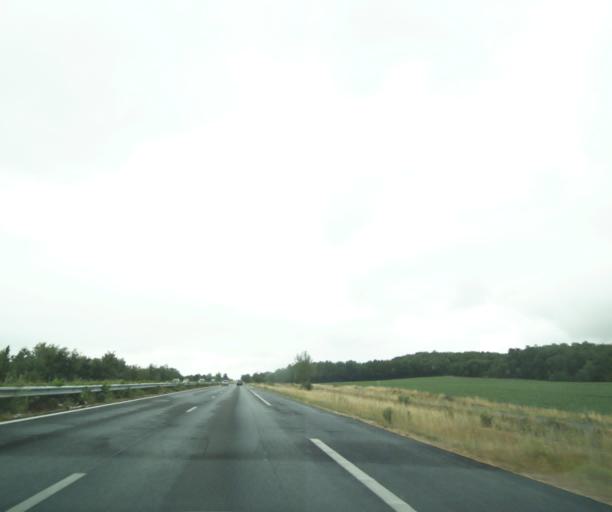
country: FR
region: Midi-Pyrenees
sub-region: Departement du Tarn
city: Lisle-sur-Tarn
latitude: 43.8291
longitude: 1.8259
